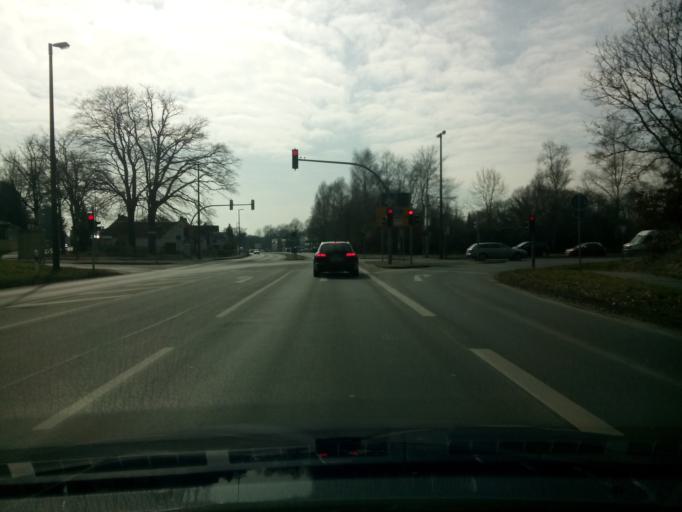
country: DE
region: Lower Saxony
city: Ritterhude
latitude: 53.1878
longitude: 8.7086
